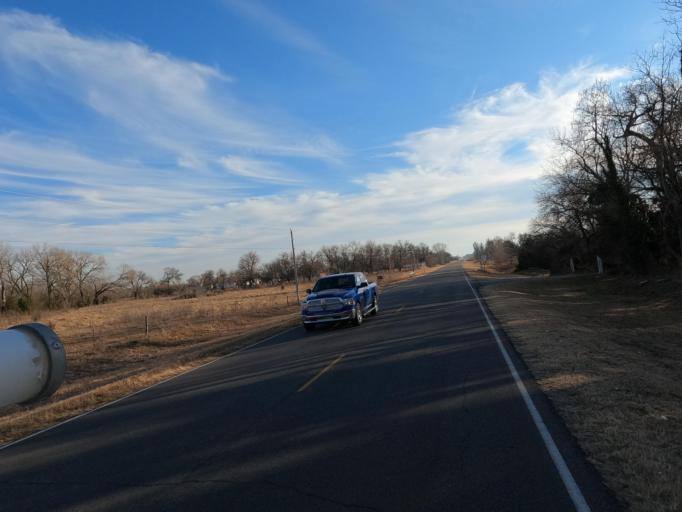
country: US
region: Kansas
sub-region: Reno County
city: Buhler
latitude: 38.1175
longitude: -97.7756
